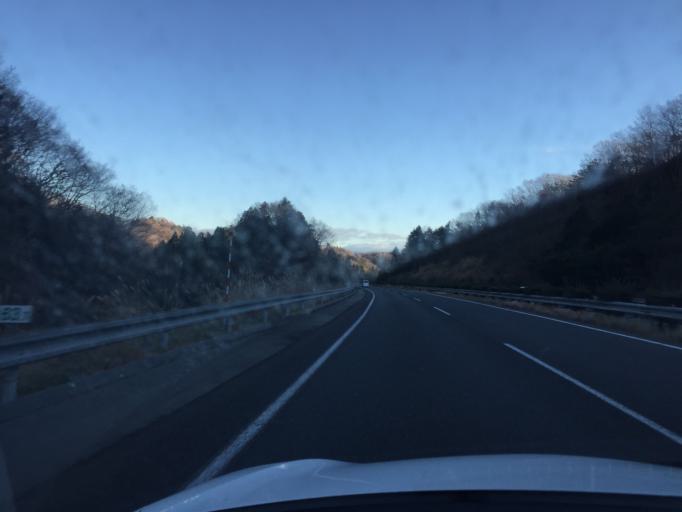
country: JP
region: Fukushima
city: Iwaki
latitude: 36.9700
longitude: 140.7908
